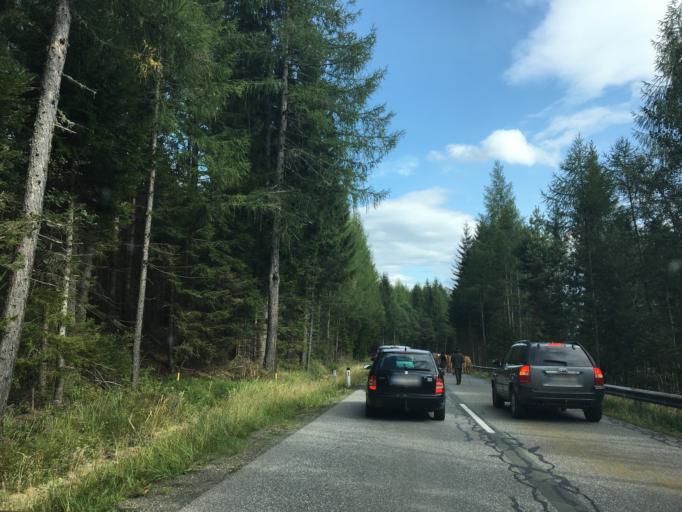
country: AT
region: Styria
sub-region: Politischer Bezirk Deutschlandsberg
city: Kloster
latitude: 46.8296
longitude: 15.0669
